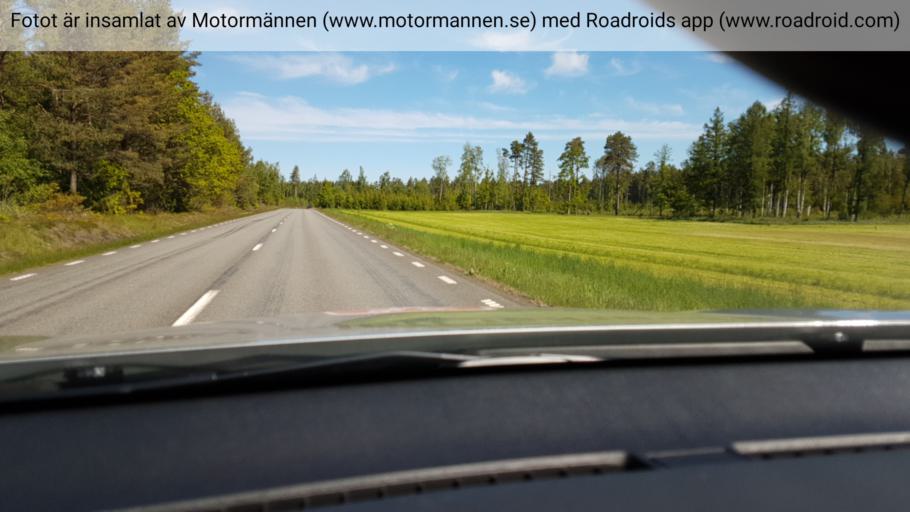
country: SE
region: Vaestra Goetaland
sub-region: Hjo Kommun
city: Hjo
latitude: 58.3845
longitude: 14.3517
